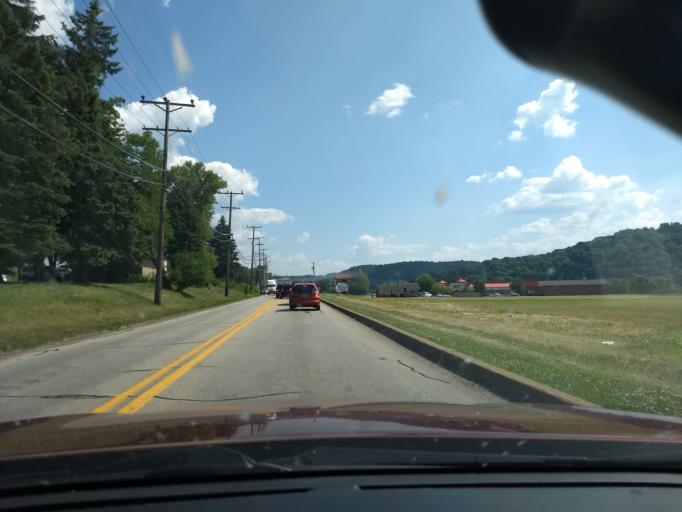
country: US
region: Pennsylvania
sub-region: Westmoreland County
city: Trafford
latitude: 40.3932
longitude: -79.7664
